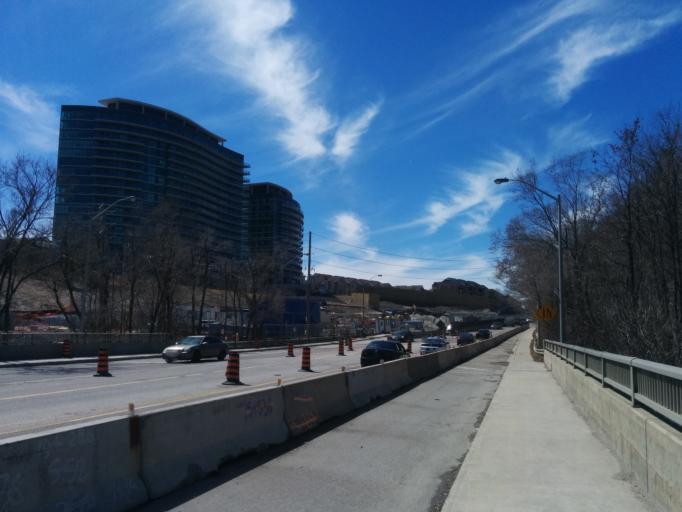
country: CA
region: Ontario
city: Toronto
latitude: 43.7163
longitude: -79.3528
